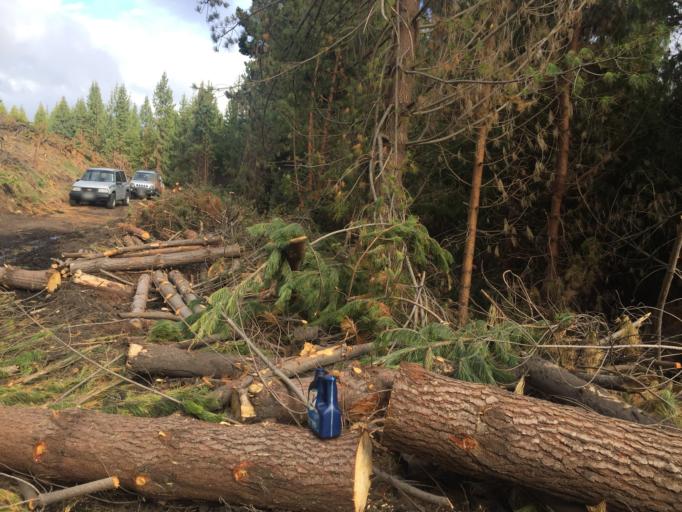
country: EC
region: Imbabura
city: Ibarra
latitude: 0.2258
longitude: -78.1252
